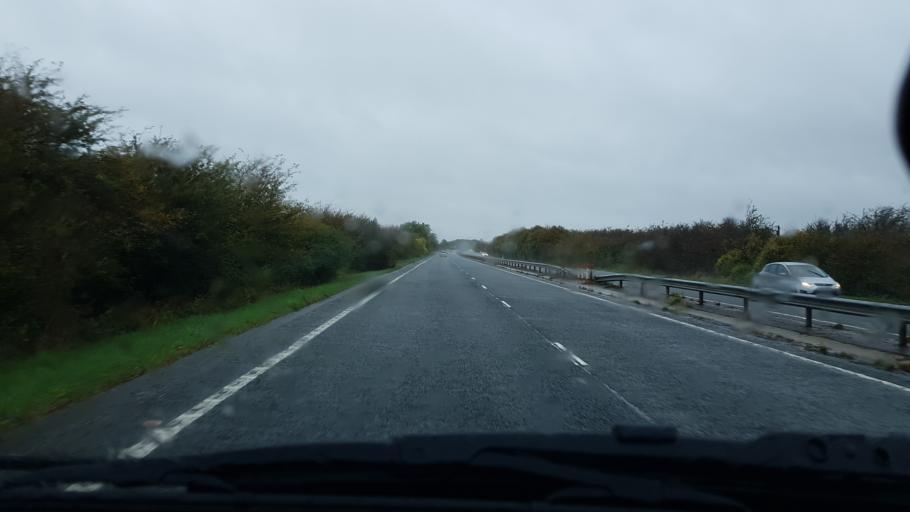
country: GB
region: England
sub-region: Oxfordshire
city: Carterton
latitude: 51.7852
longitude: -1.5668
